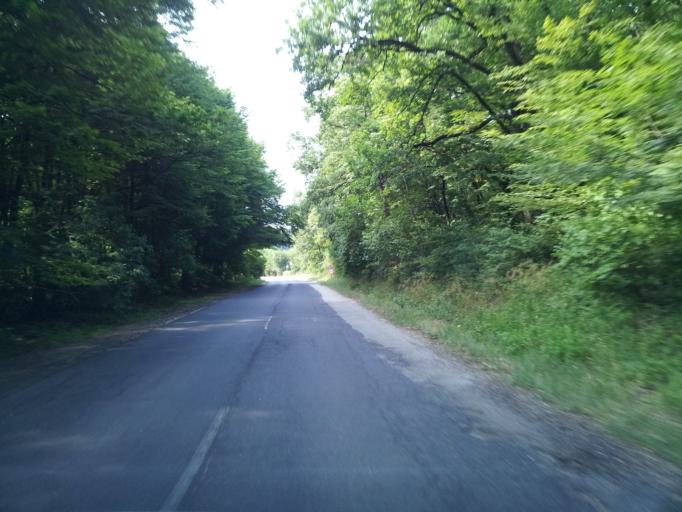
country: HU
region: Veszprem
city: Balatonfured
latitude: 46.9885
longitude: 17.8157
